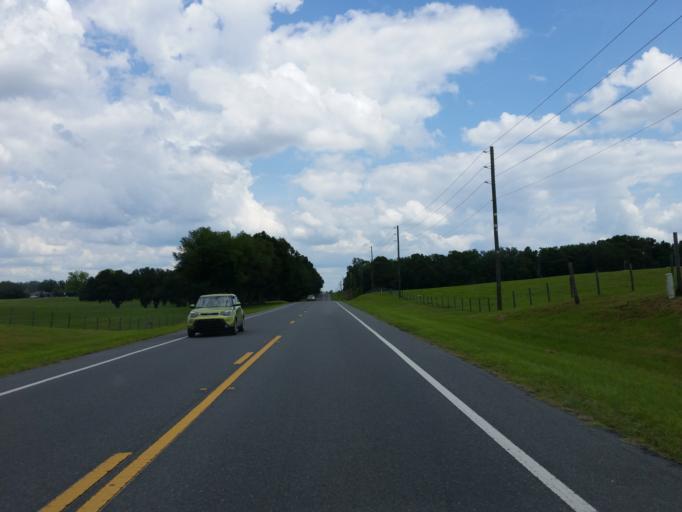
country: US
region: Florida
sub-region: Levy County
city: Williston Highlands
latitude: 29.2574
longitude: -82.4415
